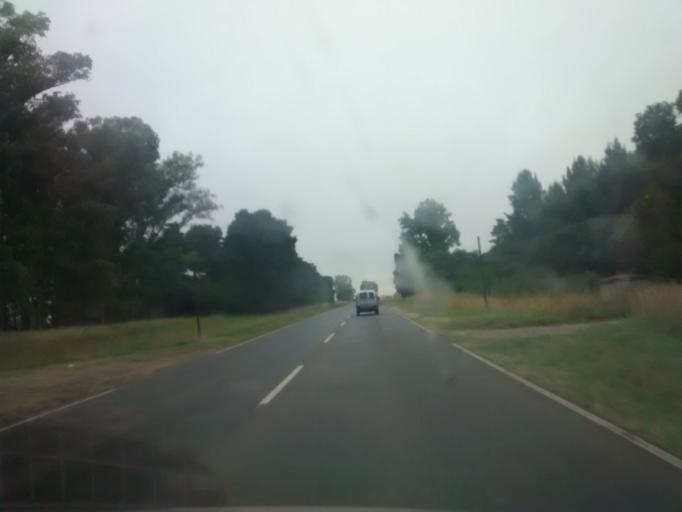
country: AR
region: Buenos Aires
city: Ranchos
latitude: -35.4420
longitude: -58.3141
